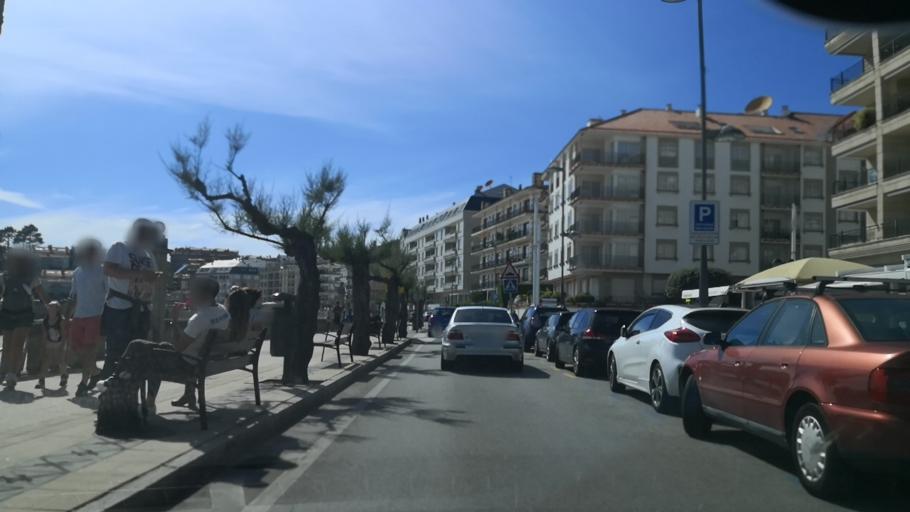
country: ES
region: Galicia
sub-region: Provincia de Pontevedra
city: Sanxenxo
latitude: 42.4015
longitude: -8.8123
